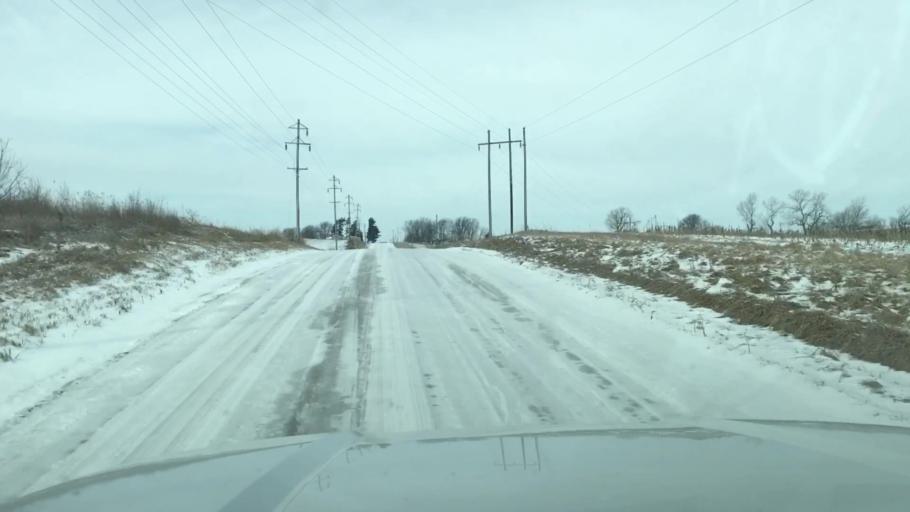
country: US
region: Missouri
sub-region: Holt County
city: Mound City
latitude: 40.1301
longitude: -95.0826
